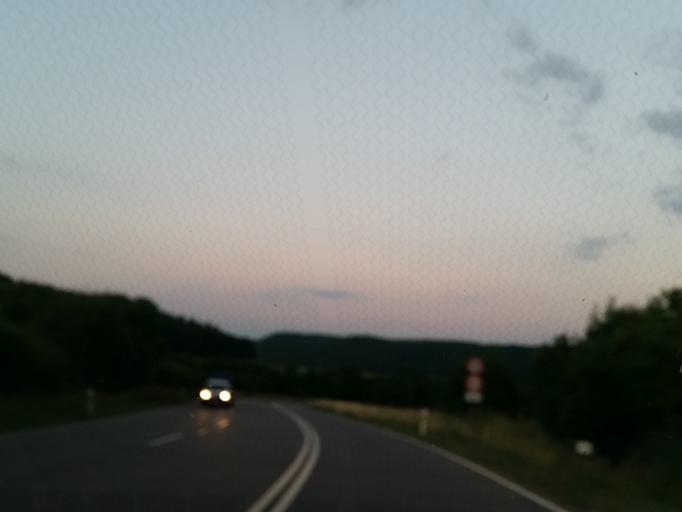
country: DE
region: Saarland
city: Schmelz
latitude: 49.4719
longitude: 6.8359
